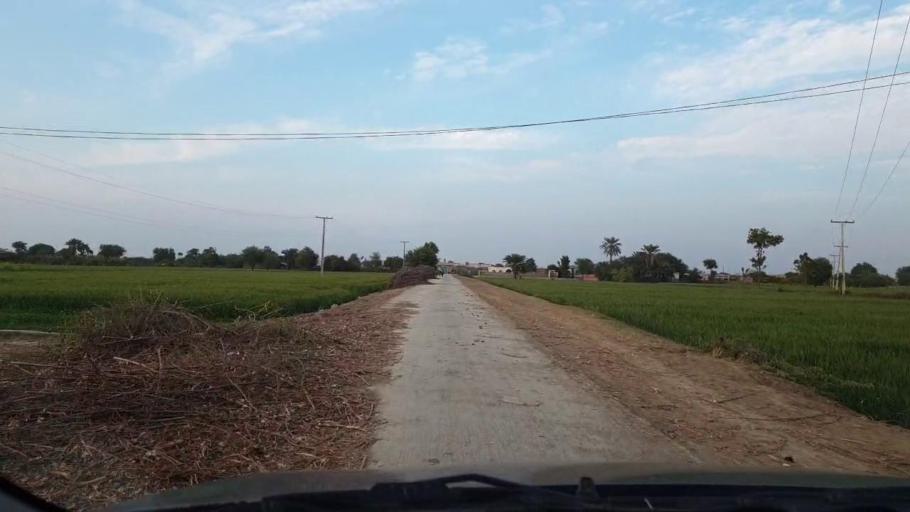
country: PK
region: Sindh
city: Jhol
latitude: 25.9860
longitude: 68.8656
